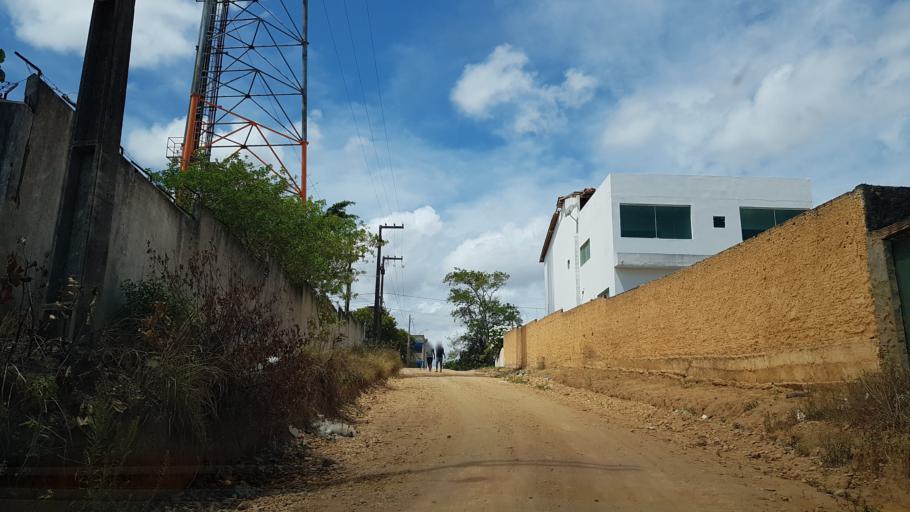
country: BR
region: Alagoas
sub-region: Penedo
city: Penedo
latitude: -10.2850
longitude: -36.5701
